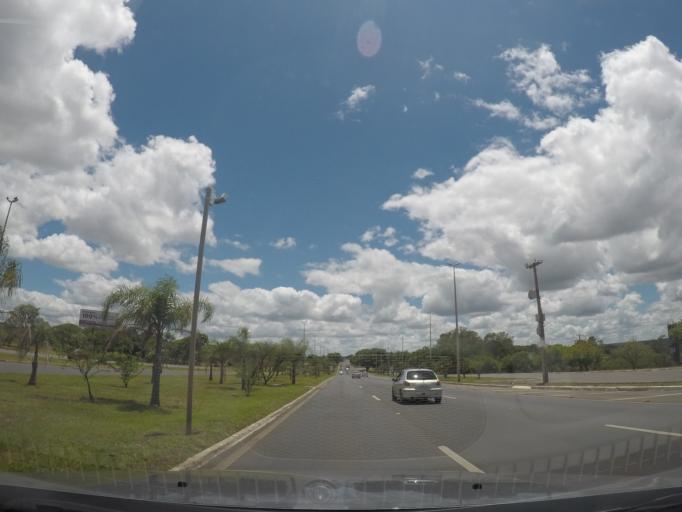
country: BR
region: Federal District
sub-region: Brasilia
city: Brasilia
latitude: -15.8447
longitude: -47.9396
